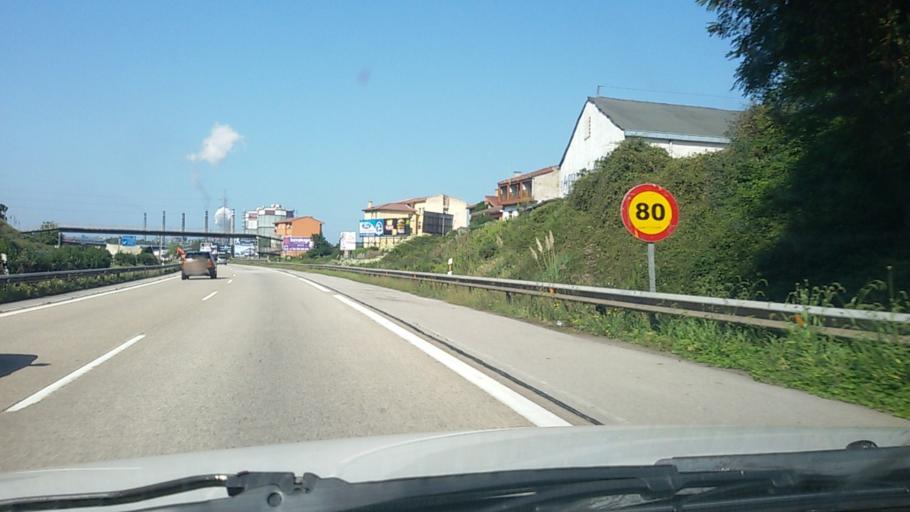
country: ES
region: Asturias
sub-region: Province of Asturias
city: Aviles
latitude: 43.5529
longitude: -5.8849
